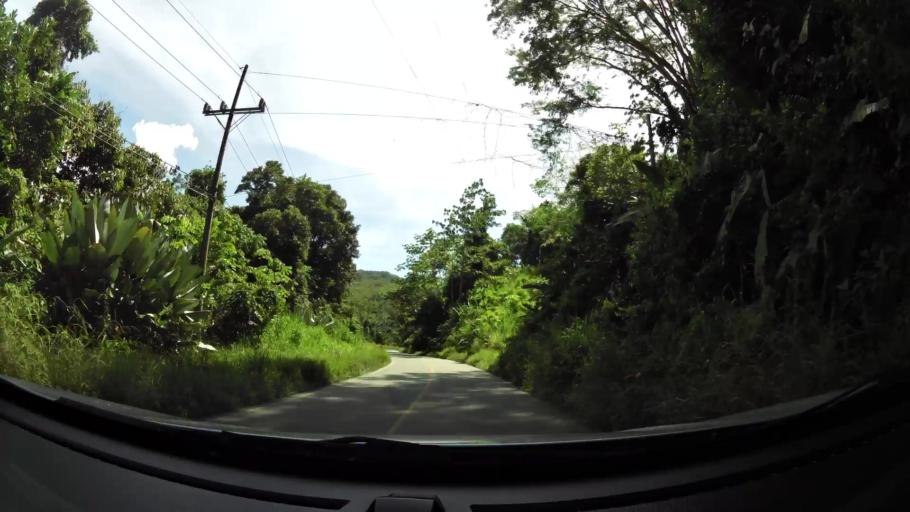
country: CR
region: San Jose
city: San Isidro
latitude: 9.2757
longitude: -83.8598
